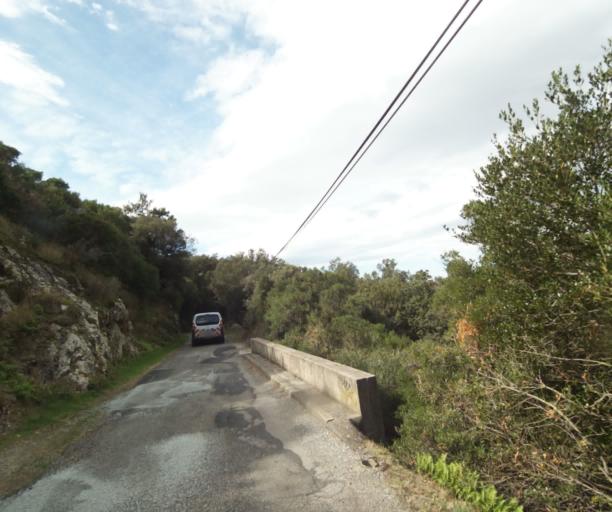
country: FR
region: Languedoc-Roussillon
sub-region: Departement des Pyrenees-Orientales
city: Sorede
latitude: 42.5226
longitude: 2.9886
